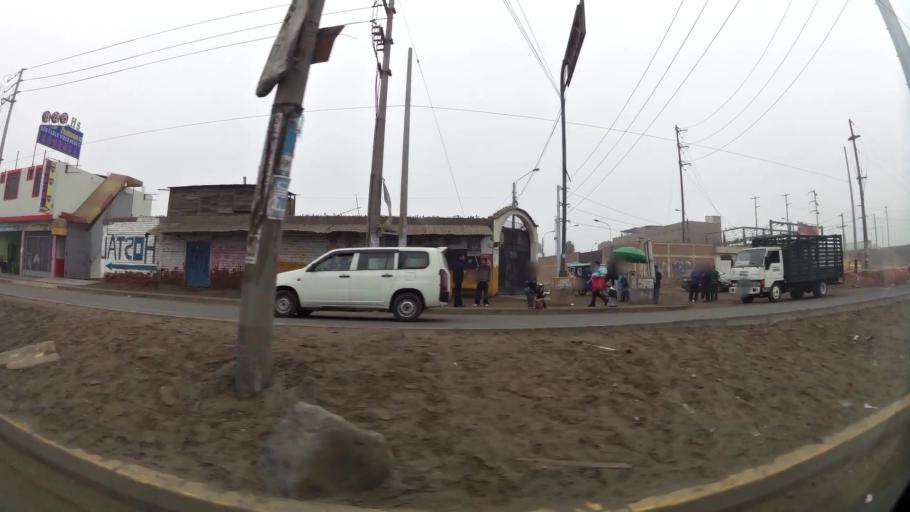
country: PE
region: Lima
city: Ventanilla
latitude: -11.8375
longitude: -77.1110
